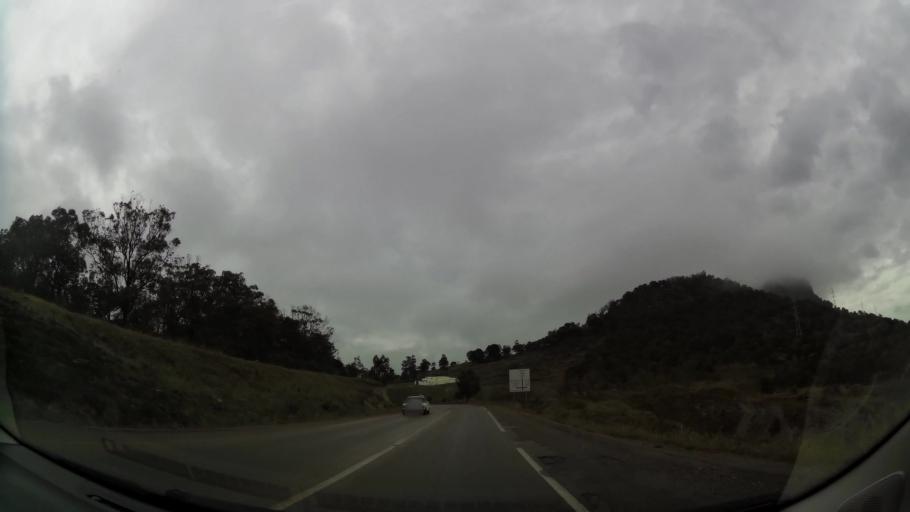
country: MA
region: Oriental
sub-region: Nador
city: Nador
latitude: 35.1515
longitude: -3.0202
